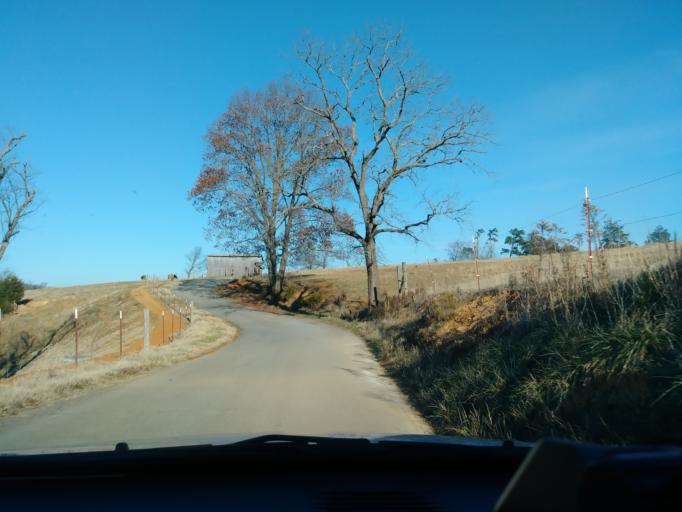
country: US
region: Tennessee
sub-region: Greene County
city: Greeneville
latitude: 36.0859
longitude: -82.9050
